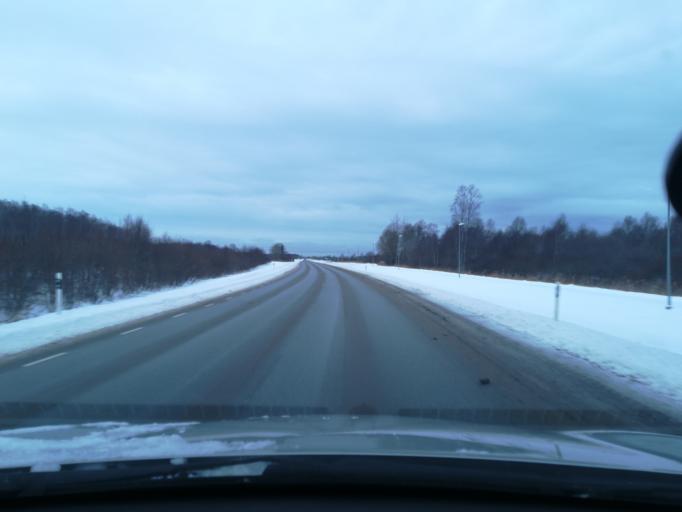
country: EE
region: Harju
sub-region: Harku vald
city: Tabasalu
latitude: 59.4558
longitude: 24.4194
